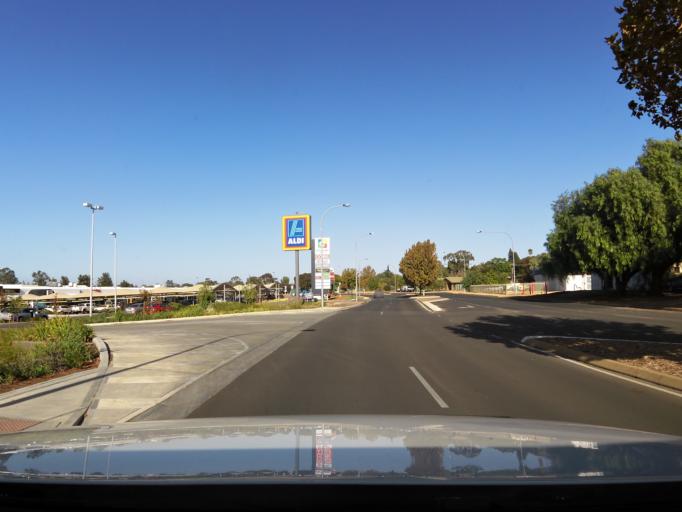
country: AU
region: South Australia
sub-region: Berri and Barmera
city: Berri
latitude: -34.2788
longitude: 140.6093
